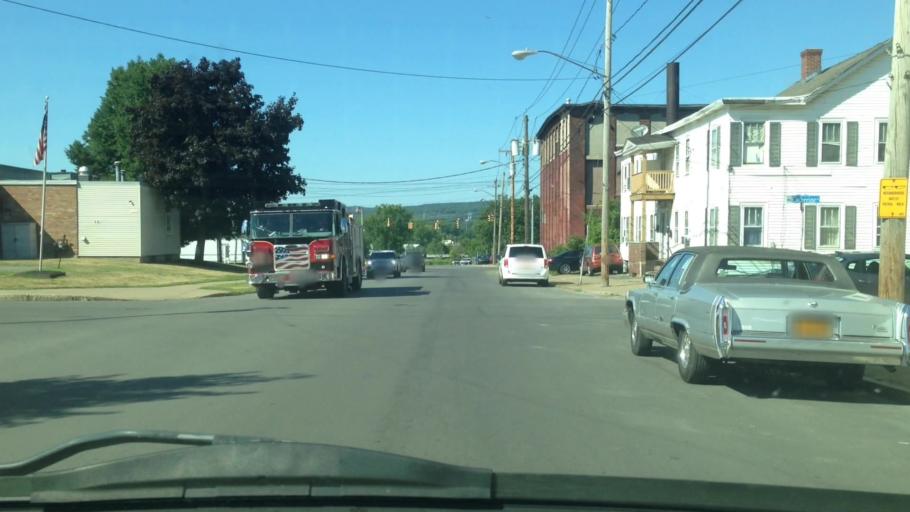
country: US
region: New York
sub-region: Oneida County
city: Utica
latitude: 43.0997
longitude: -75.2171
